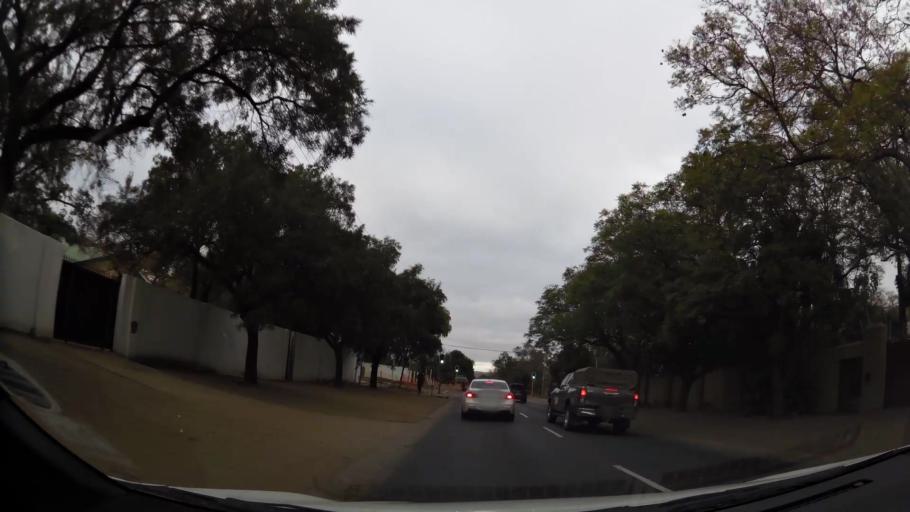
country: ZA
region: Limpopo
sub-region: Capricorn District Municipality
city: Polokwane
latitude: -23.9036
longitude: 29.4571
